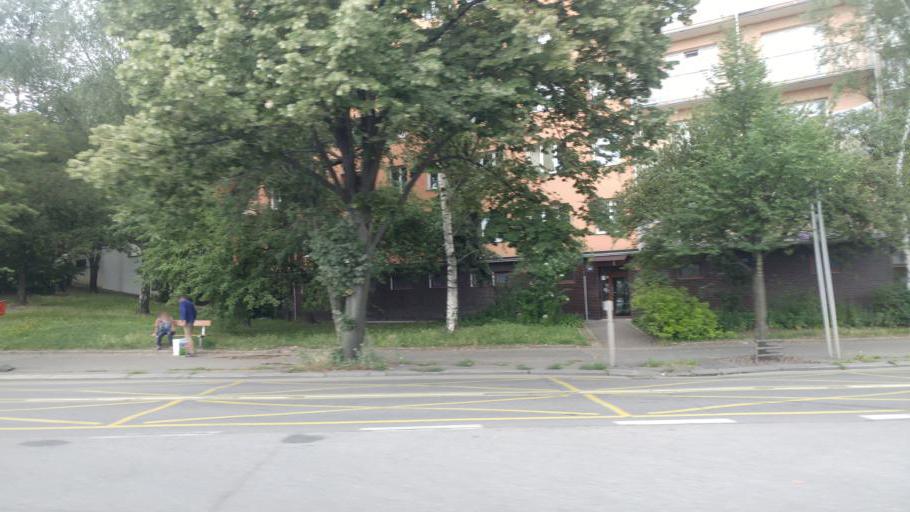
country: CZ
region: Praha
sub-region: Praha 9
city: Prosek
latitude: 50.0933
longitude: 14.4971
